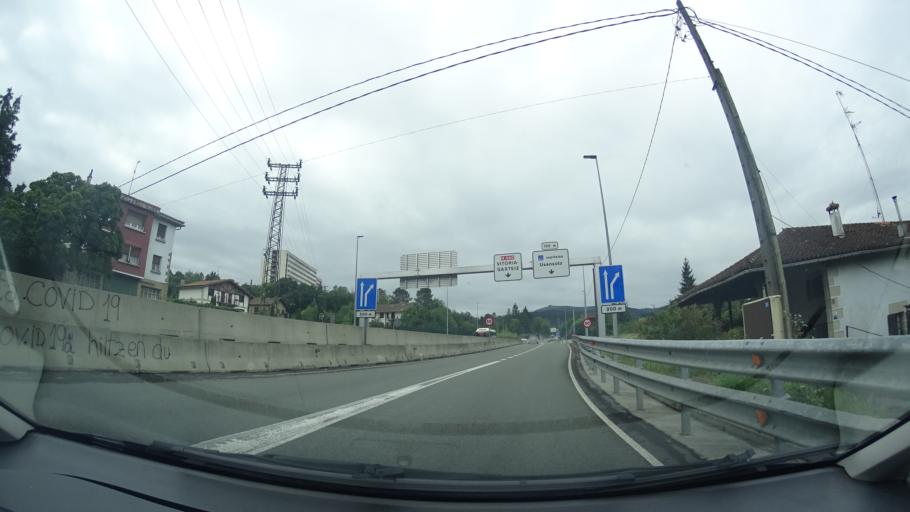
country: ES
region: Basque Country
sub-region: Bizkaia
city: Galdakao
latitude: 43.2262
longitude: -2.8199
